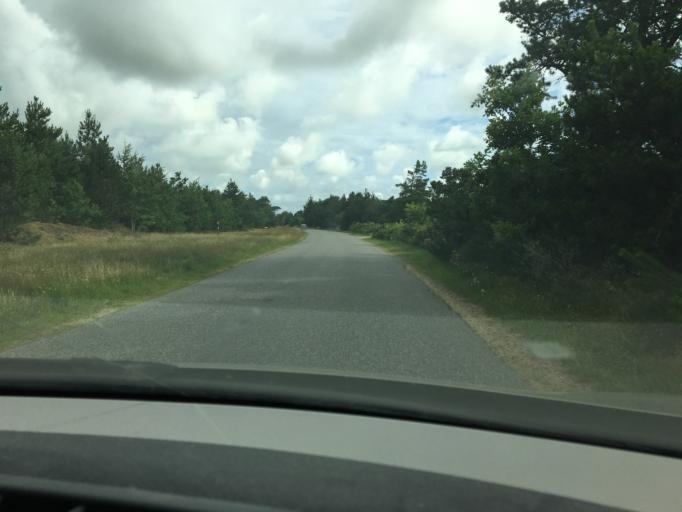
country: DK
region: Central Jutland
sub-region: Ringkobing-Skjern Kommune
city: Hvide Sande
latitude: 55.8206
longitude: 8.2153
